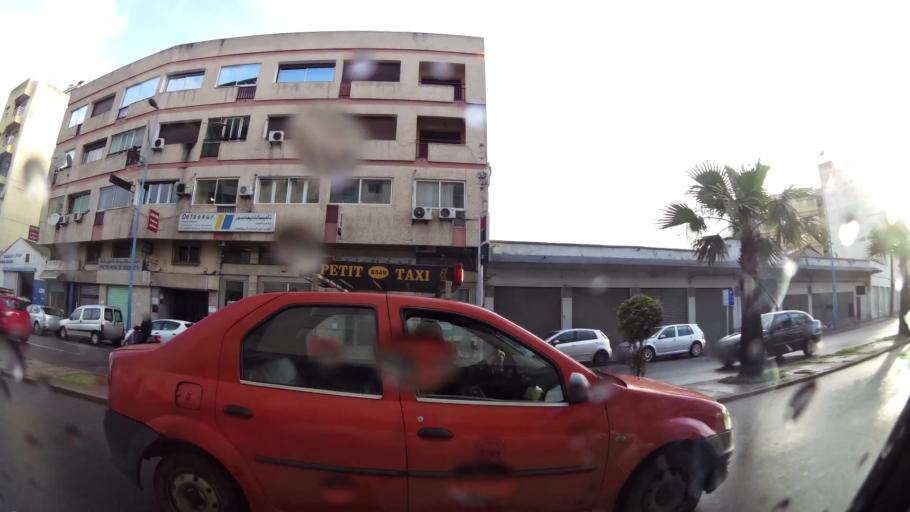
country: MA
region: Grand Casablanca
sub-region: Casablanca
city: Casablanca
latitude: 33.5881
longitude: -7.5997
